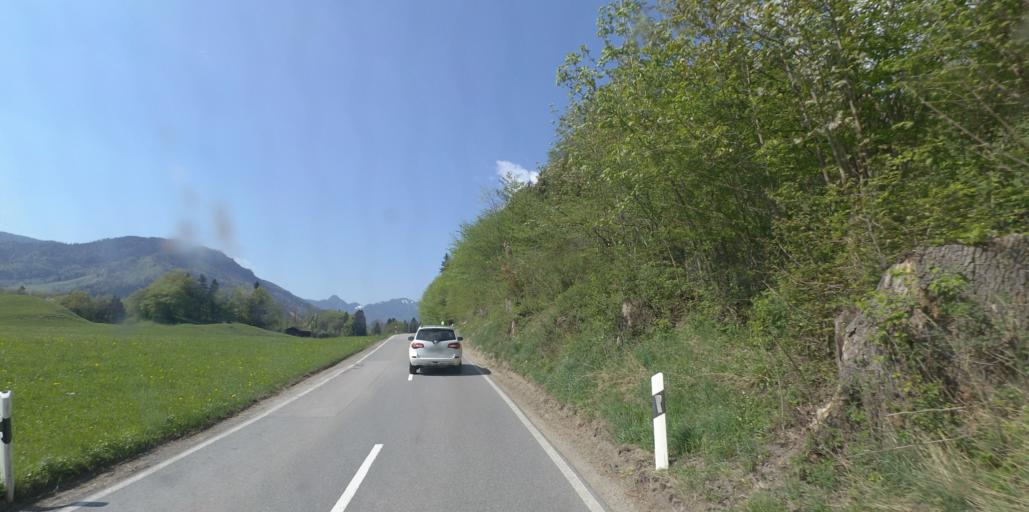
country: DE
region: Bavaria
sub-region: Upper Bavaria
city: Marquartstein
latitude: 47.7477
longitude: 12.4594
